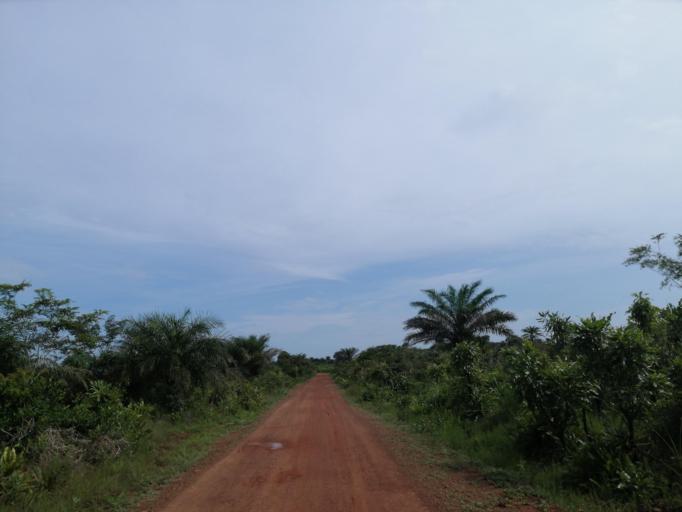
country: SL
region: Northern Province
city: Port Loko
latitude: 8.7709
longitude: -12.9141
